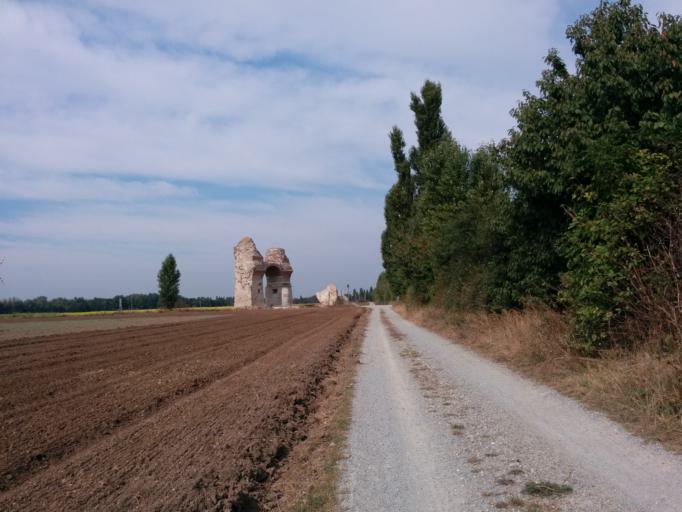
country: AT
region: Lower Austria
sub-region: Politischer Bezirk Bruck an der Leitha
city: Petronell-Carnuntum
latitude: 48.1032
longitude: 16.8551
